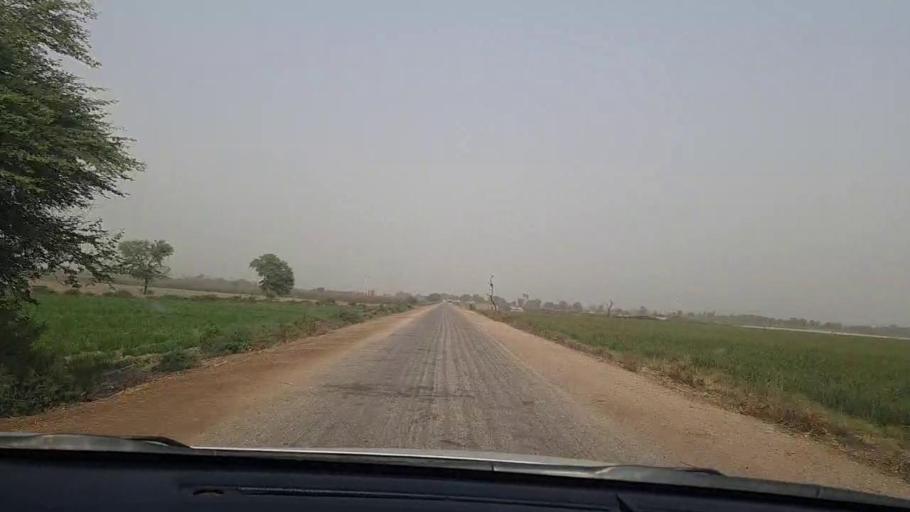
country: PK
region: Sindh
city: Pithoro
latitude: 25.4044
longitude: 69.3891
